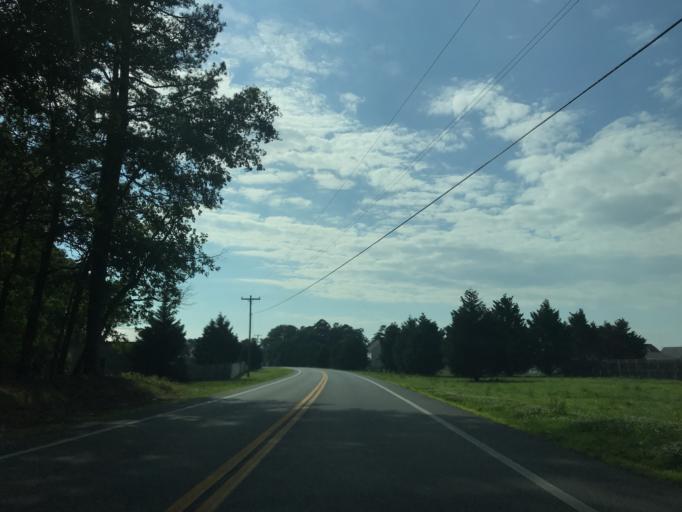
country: US
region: Maryland
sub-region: Wicomico County
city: Hebron
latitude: 38.4644
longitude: -75.7083
